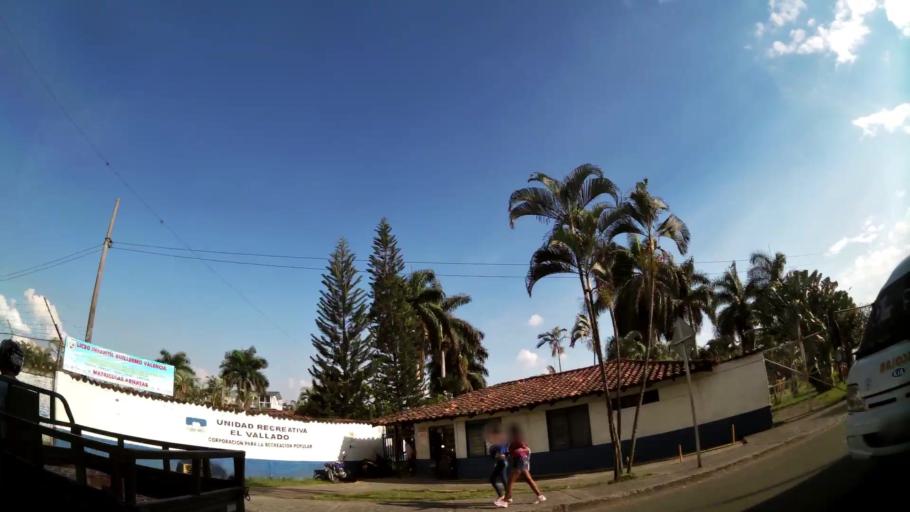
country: CO
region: Valle del Cauca
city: Cali
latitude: 3.4061
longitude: -76.4992
